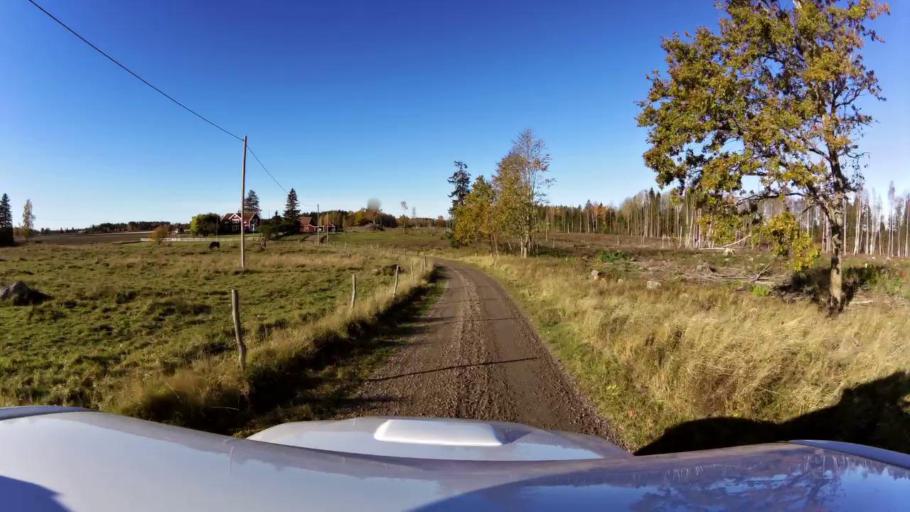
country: SE
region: OEstergoetland
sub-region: Linkopings Kommun
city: Ljungsbro
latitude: 58.5137
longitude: 15.4027
